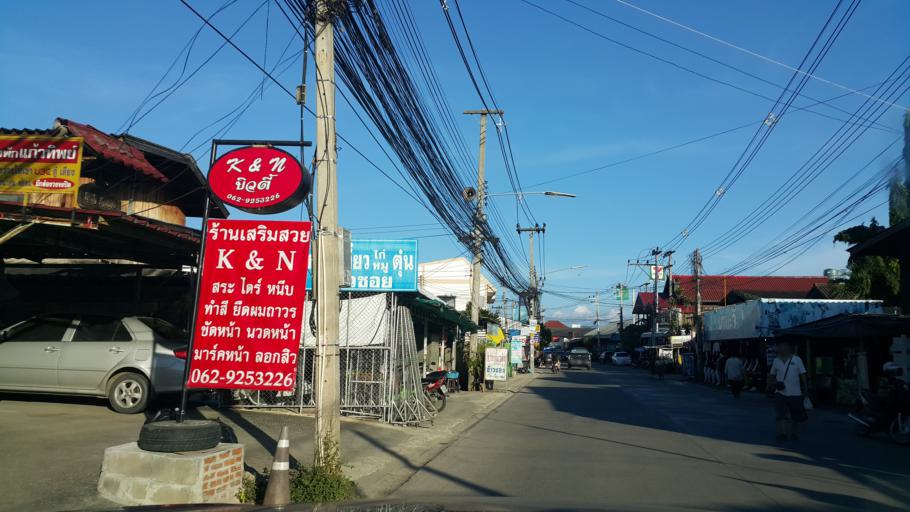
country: TH
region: Lamphun
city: Lamphun
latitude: 18.5996
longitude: 99.0262
